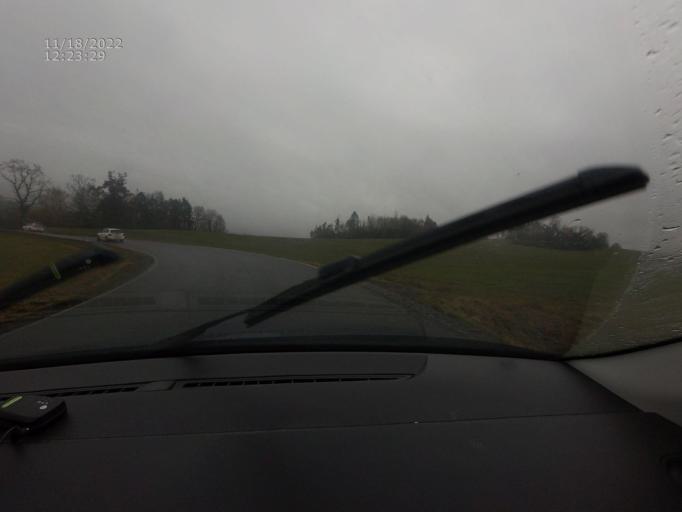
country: CZ
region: Plzensky
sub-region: Okres Plzen-Jih
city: Nepomuk
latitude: 49.4482
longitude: 13.5344
